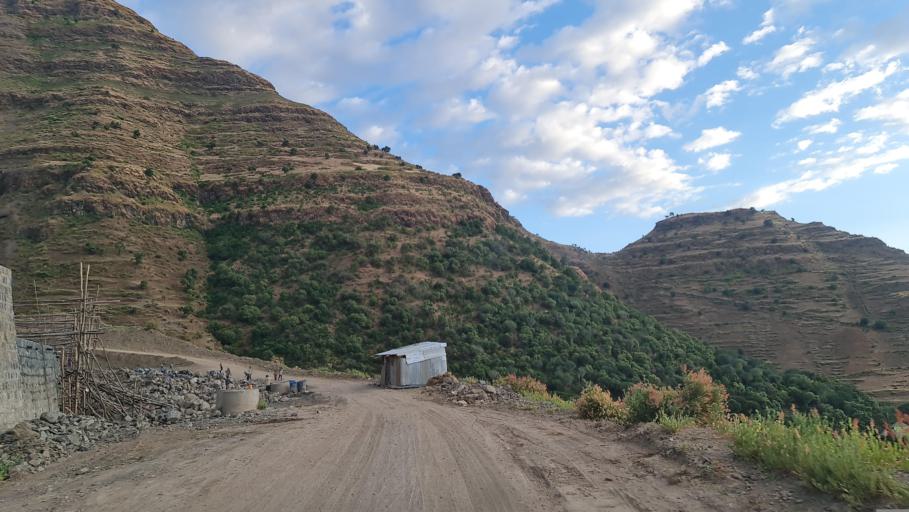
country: ET
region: Amhara
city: Debark'
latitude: 13.0116
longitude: 38.0464
